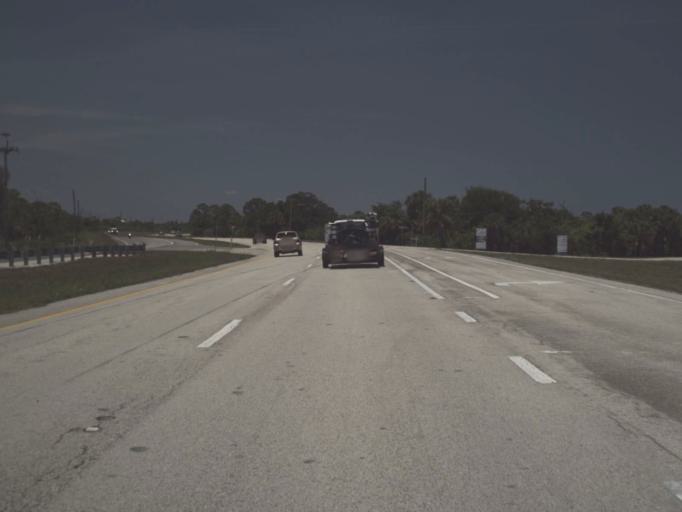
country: US
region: Florida
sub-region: Brevard County
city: Grant-Valkaria
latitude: 27.9689
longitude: -80.5445
